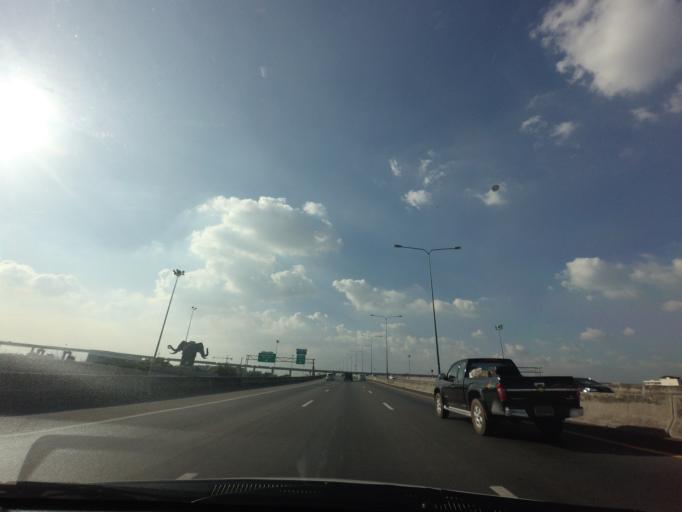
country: TH
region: Samut Prakan
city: Samut Prakan
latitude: 13.6285
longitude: 100.5923
